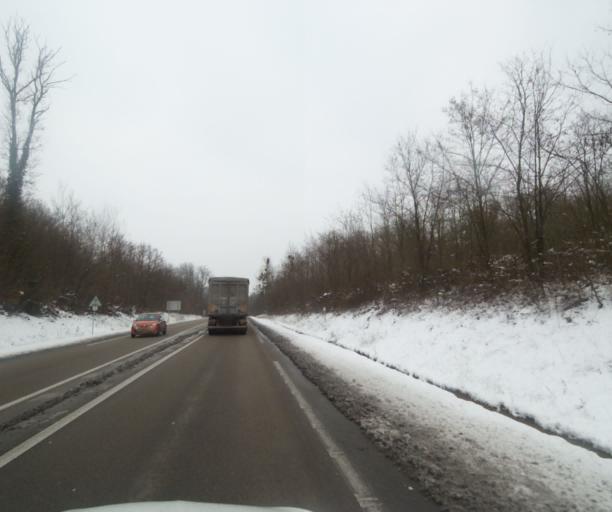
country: FR
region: Champagne-Ardenne
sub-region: Departement de la Haute-Marne
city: Saint-Dizier
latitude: 48.6063
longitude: 4.9112
